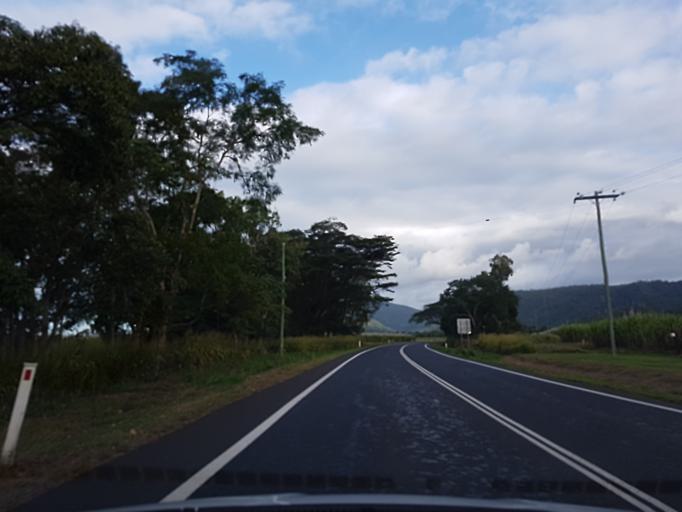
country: AU
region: Queensland
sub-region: Cairns
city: Port Douglas
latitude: -16.5411
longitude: 145.4709
